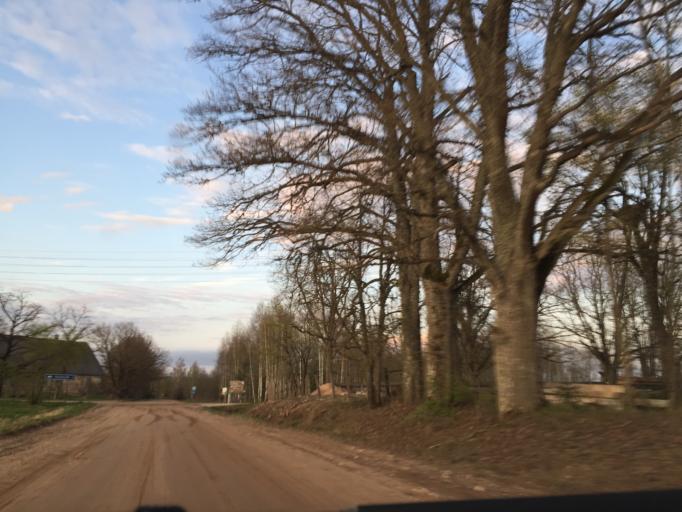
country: LV
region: Gulbenes Rajons
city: Gulbene
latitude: 57.2469
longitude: 26.8819
